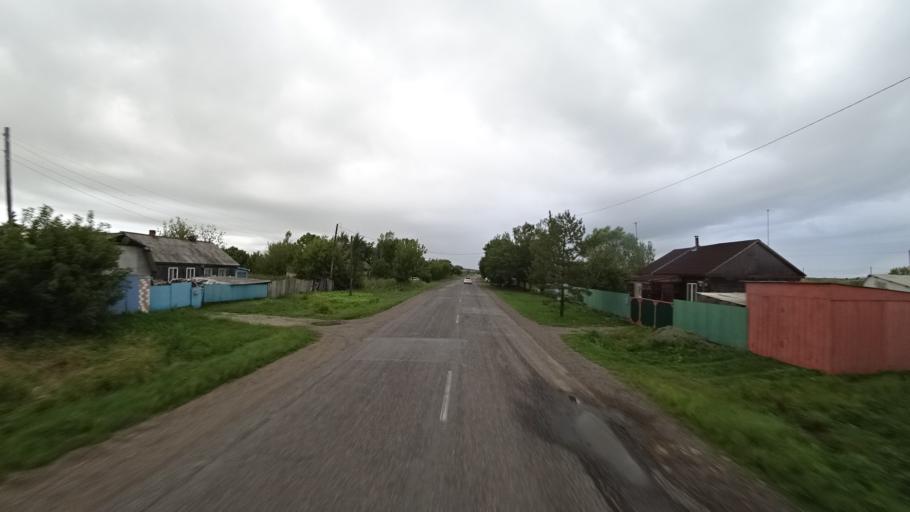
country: RU
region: Primorskiy
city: Chernigovka
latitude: 44.3539
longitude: 132.5657
